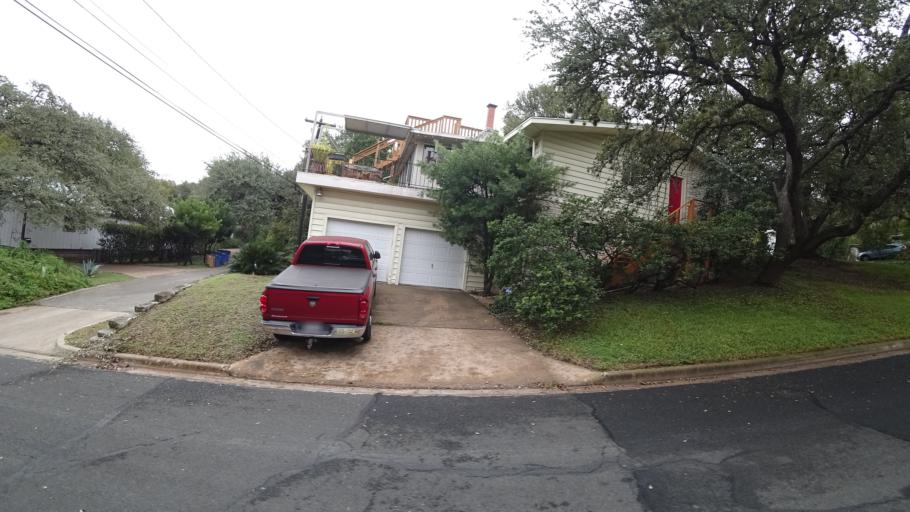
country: US
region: Texas
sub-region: Travis County
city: Rollingwood
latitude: 30.2592
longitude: -97.7752
